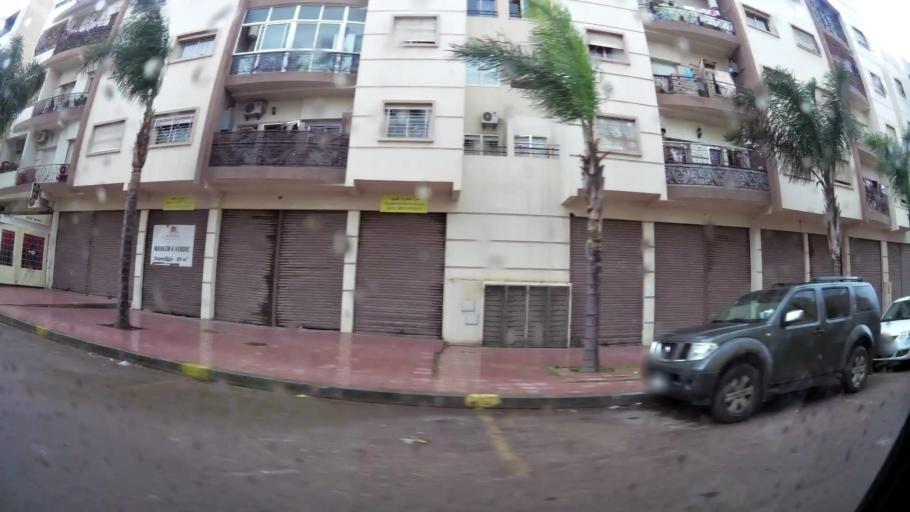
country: MA
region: Grand Casablanca
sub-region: Casablanca
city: Casablanca
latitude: 33.5511
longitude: -7.6937
